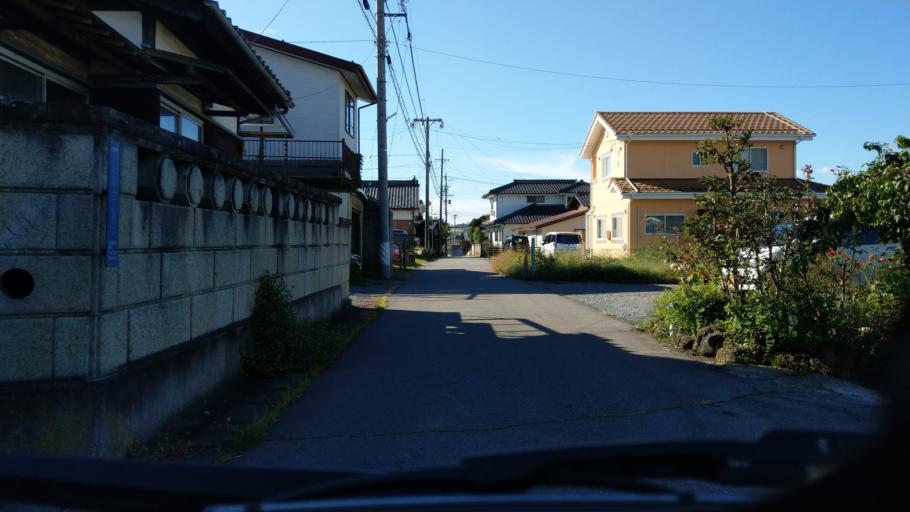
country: JP
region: Nagano
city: Komoro
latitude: 36.3270
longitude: 138.4298
